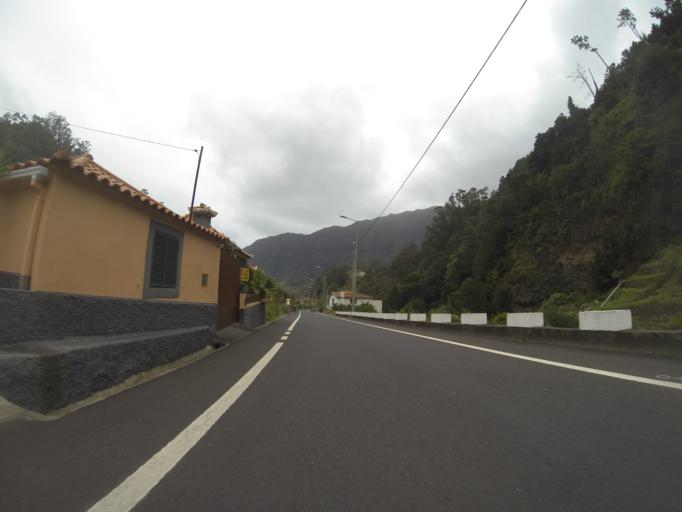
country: PT
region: Madeira
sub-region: Sao Vicente
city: Sao Vicente
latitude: 32.7832
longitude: -17.0325
